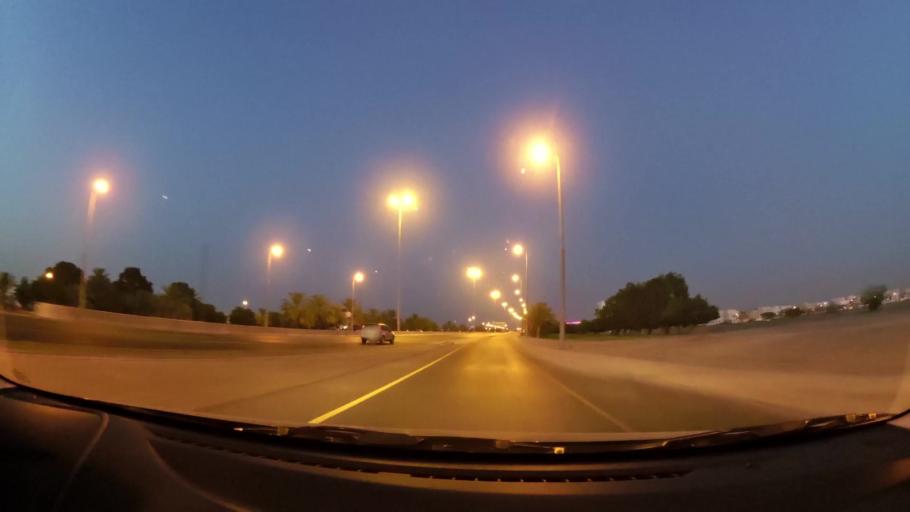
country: OM
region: Muhafazat Masqat
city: As Sib al Jadidah
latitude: 23.6573
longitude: 58.1943
